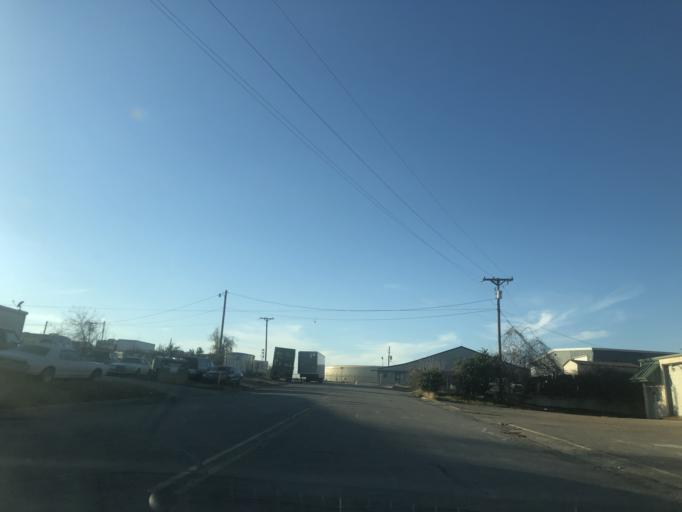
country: US
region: Texas
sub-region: Travis County
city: Wells Branch
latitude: 30.4324
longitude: -97.6811
